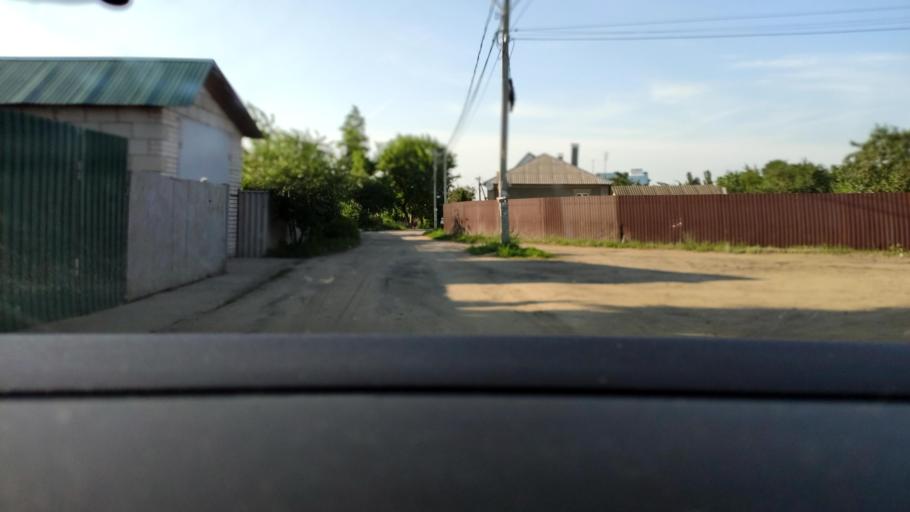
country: RU
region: Voronezj
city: Podgornoye
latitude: 51.7294
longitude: 39.1431
